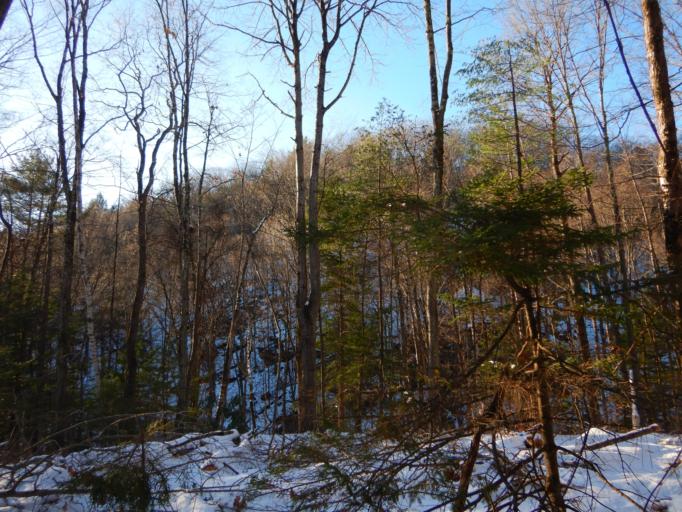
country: US
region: Vermont
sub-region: Windham County
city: West Brattleboro
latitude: 42.8841
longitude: -72.6223
